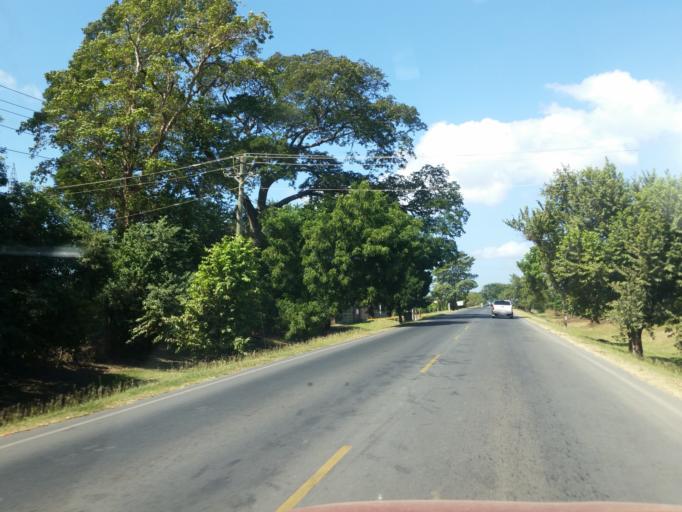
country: NI
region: Granada
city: Nandaime
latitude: 11.7491
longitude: -86.0312
